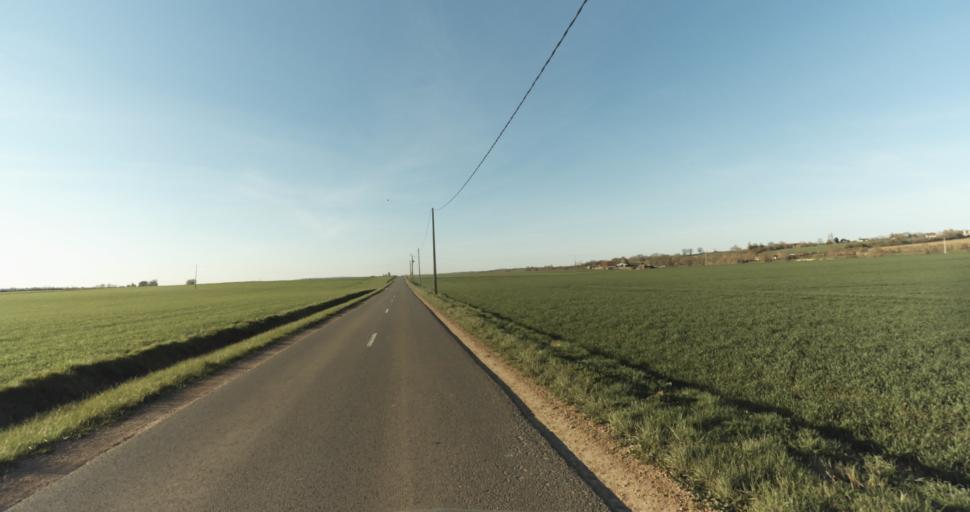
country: FR
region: Lower Normandy
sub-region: Departement du Calvados
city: Saint-Pierre-sur-Dives
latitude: 48.9985
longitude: -0.0216
